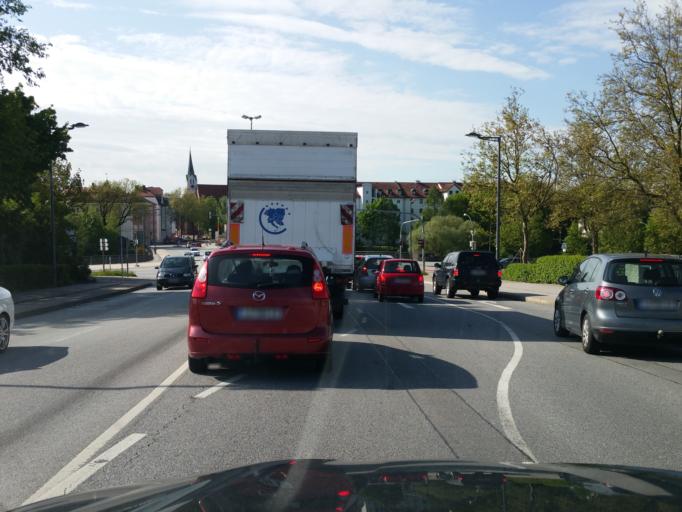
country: DE
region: Bavaria
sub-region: Lower Bavaria
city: Landshut
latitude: 48.5479
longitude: 12.1394
